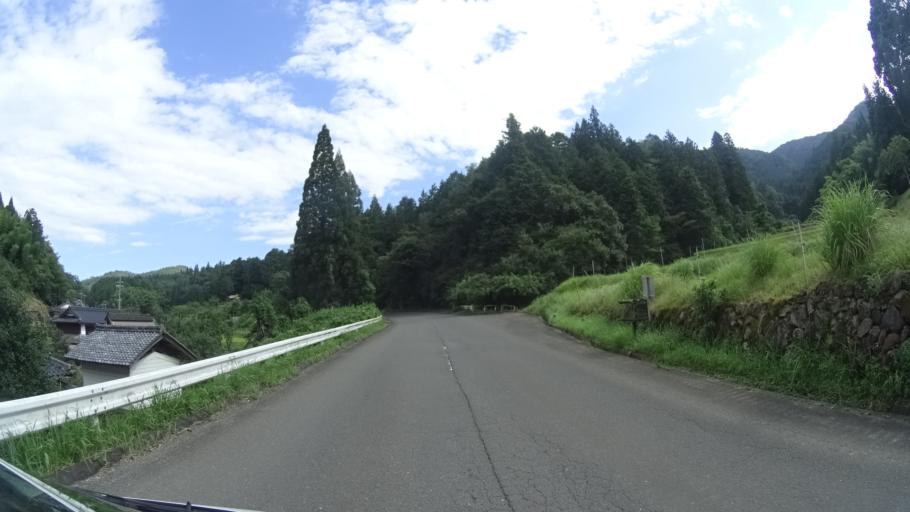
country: JP
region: Kyoto
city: Fukuchiyama
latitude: 35.3573
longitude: 135.1435
